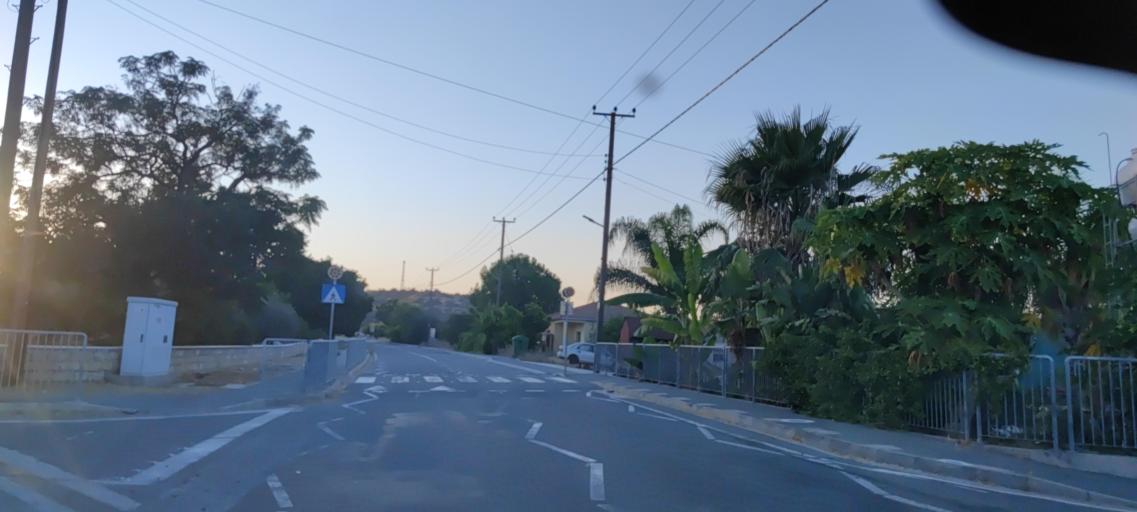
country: CY
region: Limassol
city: Sotira
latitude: 34.6764
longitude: 32.7926
